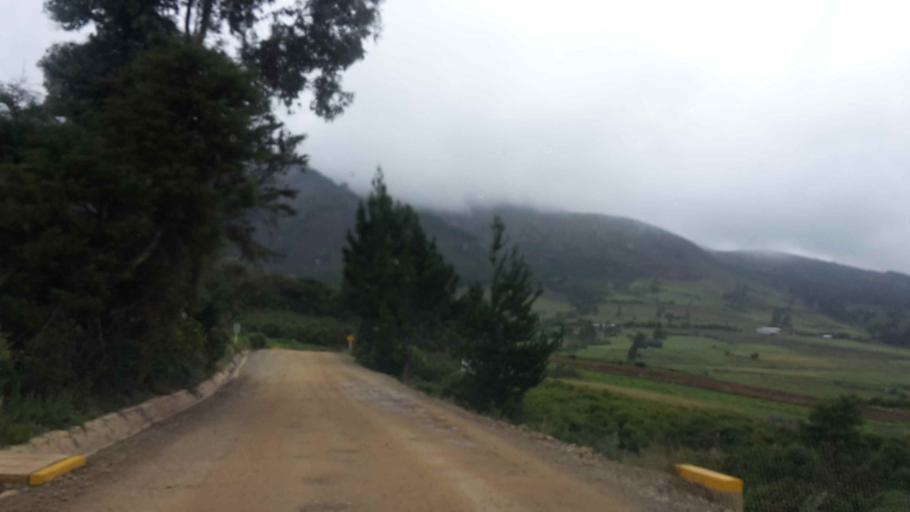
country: BO
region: Cochabamba
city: Totora
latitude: -17.5838
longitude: -65.2954
